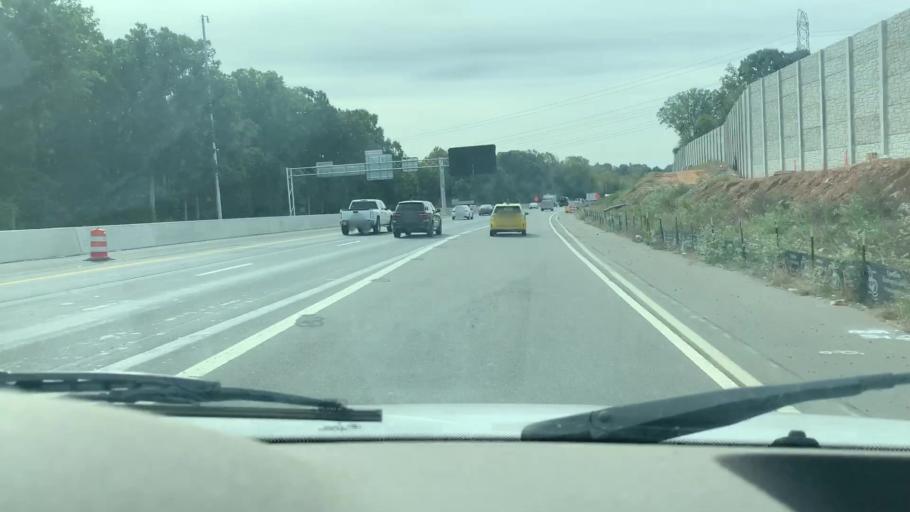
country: US
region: North Carolina
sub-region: Iredell County
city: Mooresville
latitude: 35.5761
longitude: -80.8560
